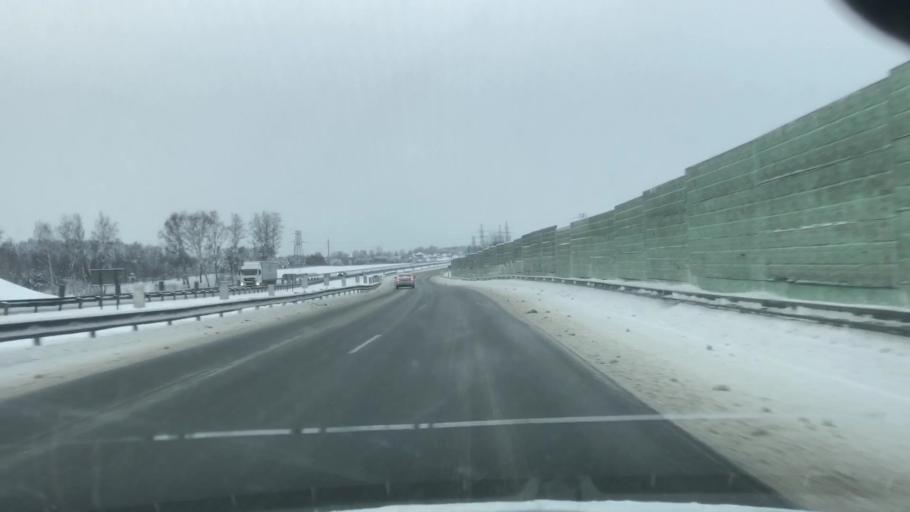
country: RU
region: Moskovskaya
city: Mikhnevo
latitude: 55.1270
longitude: 37.9345
